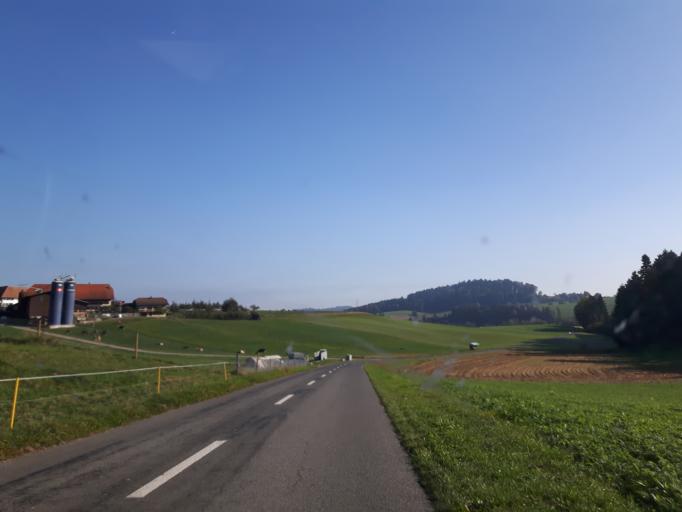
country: CH
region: Lucerne
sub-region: Willisau District
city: Pfaffnau
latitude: 47.2434
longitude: 7.8815
